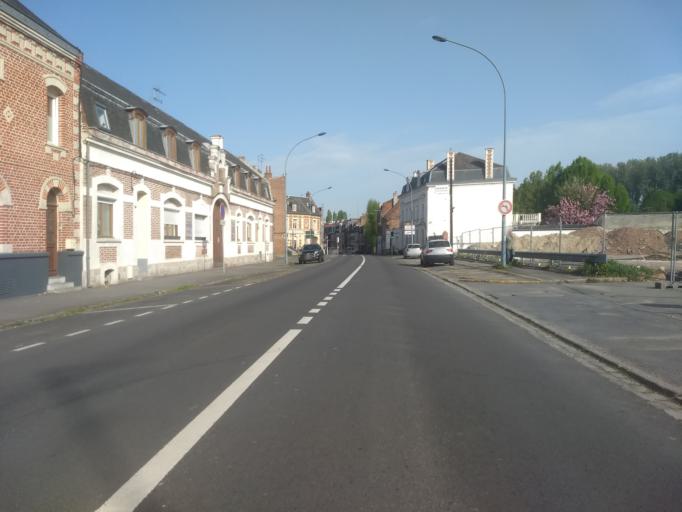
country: FR
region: Nord-Pas-de-Calais
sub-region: Departement du Pas-de-Calais
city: Sainte-Catherine
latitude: 50.2987
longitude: 2.7680
